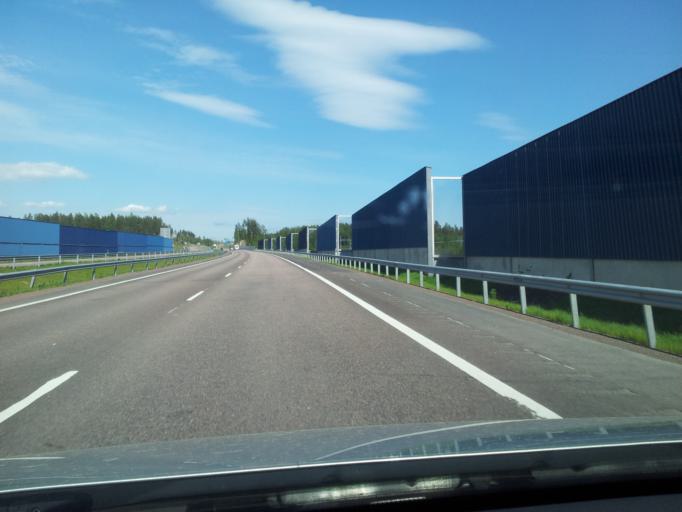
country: FI
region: Uusimaa
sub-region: Loviisa
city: Lovisa
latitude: 60.4673
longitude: 26.2255
